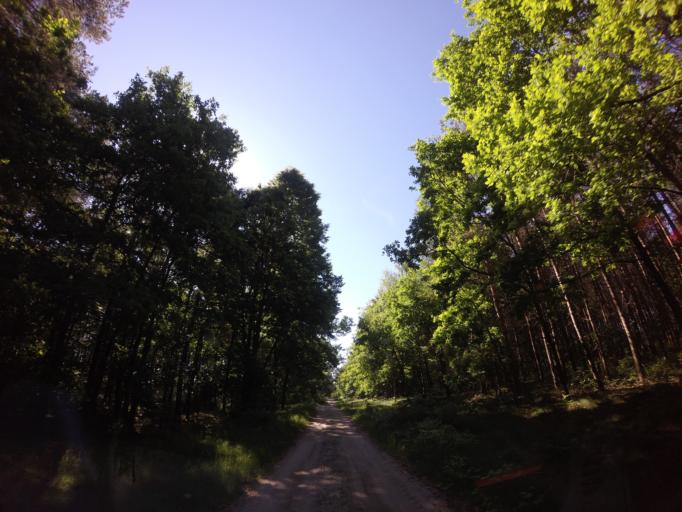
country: PL
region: West Pomeranian Voivodeship
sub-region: Powiat choszczenski
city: Drawno
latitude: 53.2242
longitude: 15.7054
